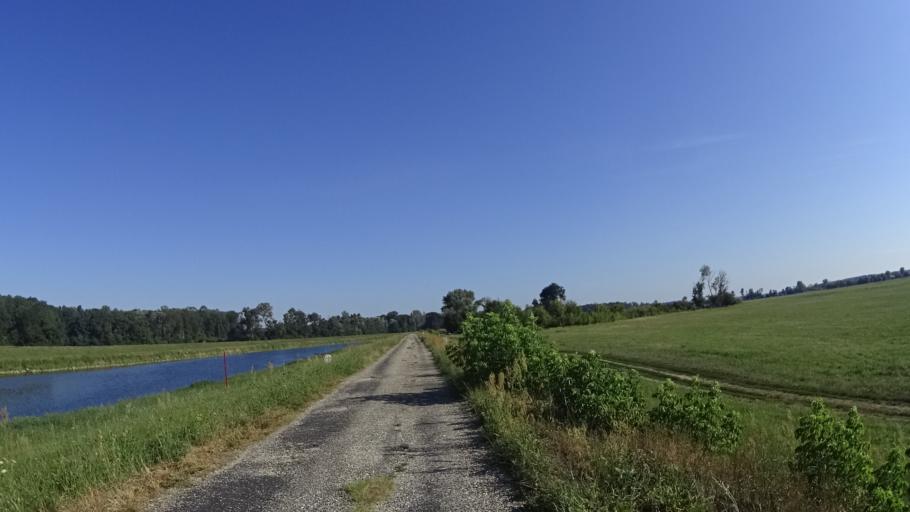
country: CZ
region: South Moravian
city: Tvrdonice
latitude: 48.7240
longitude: 17.0143
